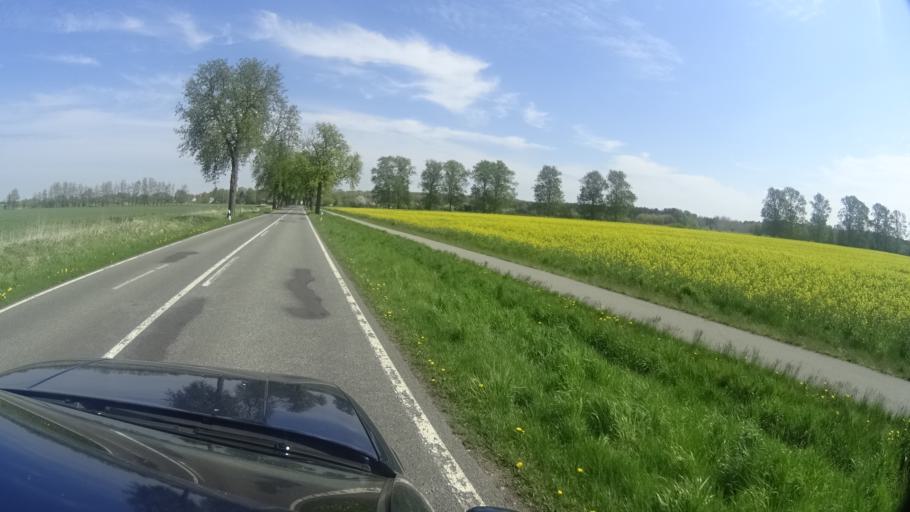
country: DE
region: Brandenburg
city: Dreetz
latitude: 52.8357
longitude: 12.4378
